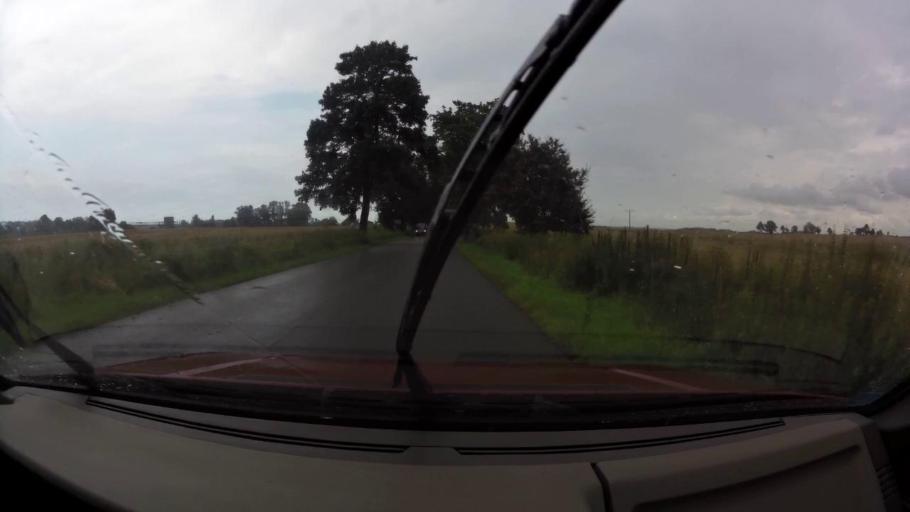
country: PL
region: West Pomeranian Voivodeship
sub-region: Koszalin
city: Koszalin
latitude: 54.1220
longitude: 16.1242
